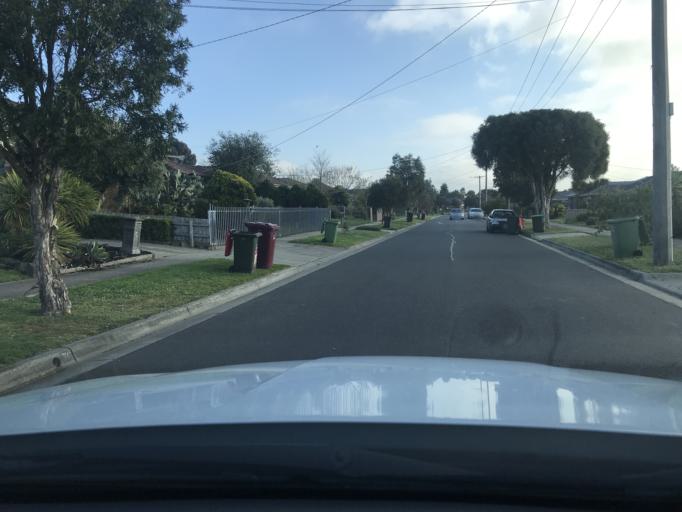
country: AU
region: Victoria
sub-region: Hume
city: Craigieburn
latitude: -37.6062
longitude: 144.9325
